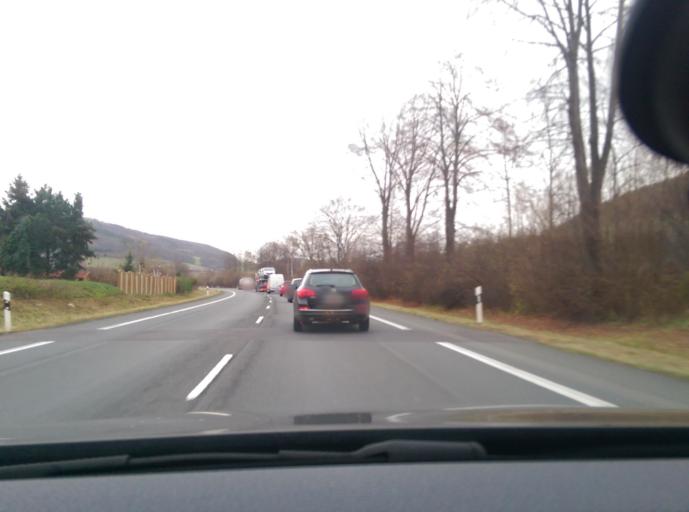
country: DE
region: Hesse
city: Witzenhausen
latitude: 51.3371
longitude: 9.8883
